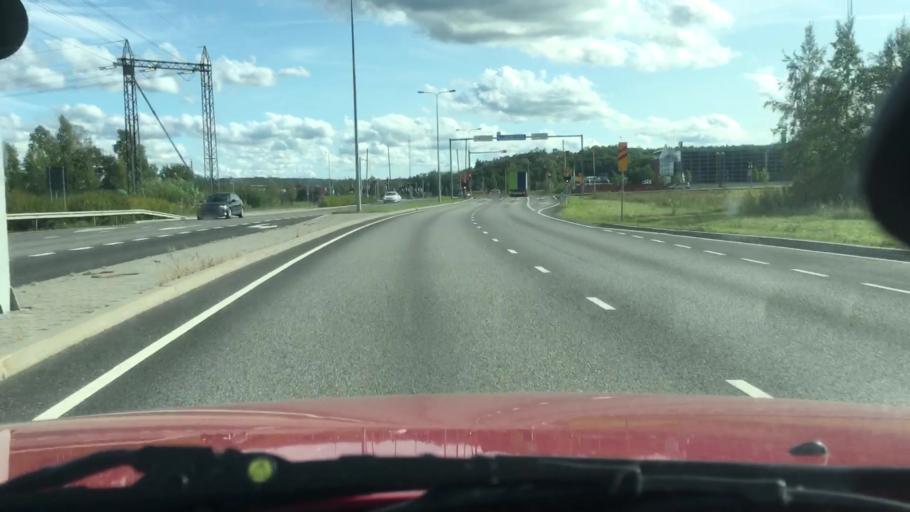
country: FI
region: Varsinais-Suomi
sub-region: Turku
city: Raisio
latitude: 60.4492
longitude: 22.2016
